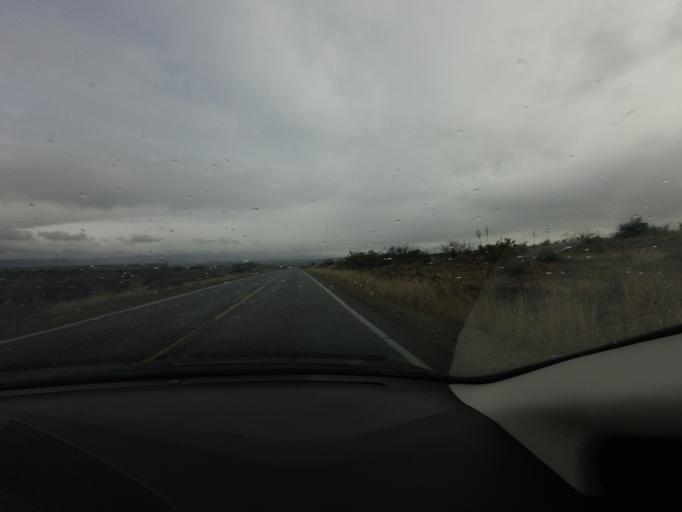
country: US
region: Arizona
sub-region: Yavapai County
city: Lake Montezuma
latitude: 34.6801
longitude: -111.8426
